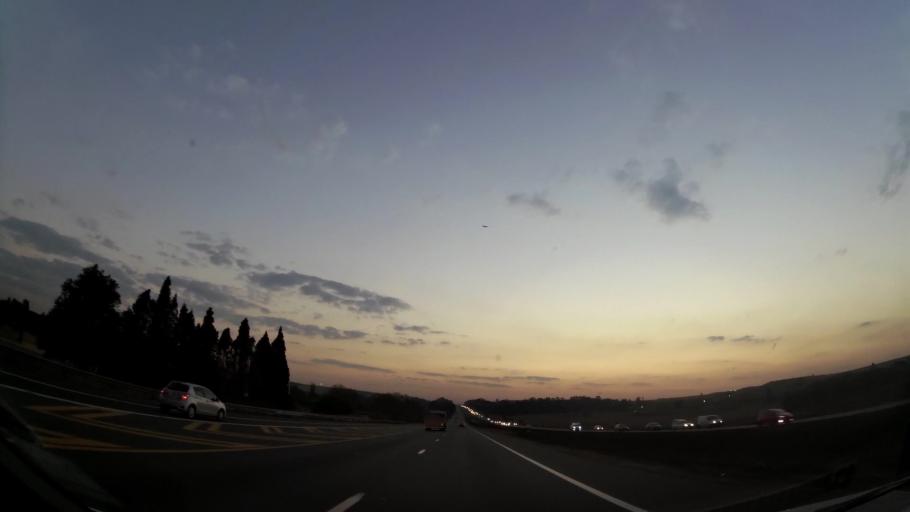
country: ZA
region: Gauteng
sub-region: Ekurhuleni Metropolitan Municipality
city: Boksburg
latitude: -26.2516
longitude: 28.2372
